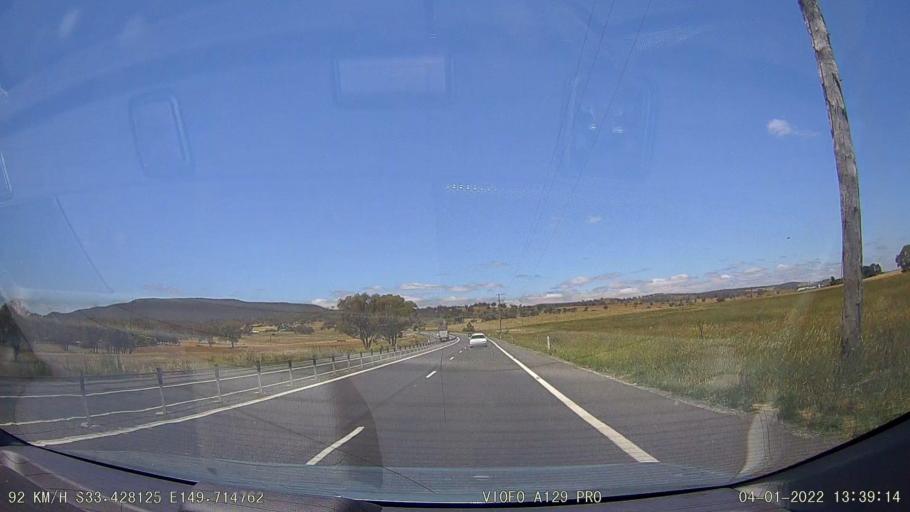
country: AU
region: New South Wales
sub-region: Bathurst Regional
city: Kelso
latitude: -33.4283
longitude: 149.7149
